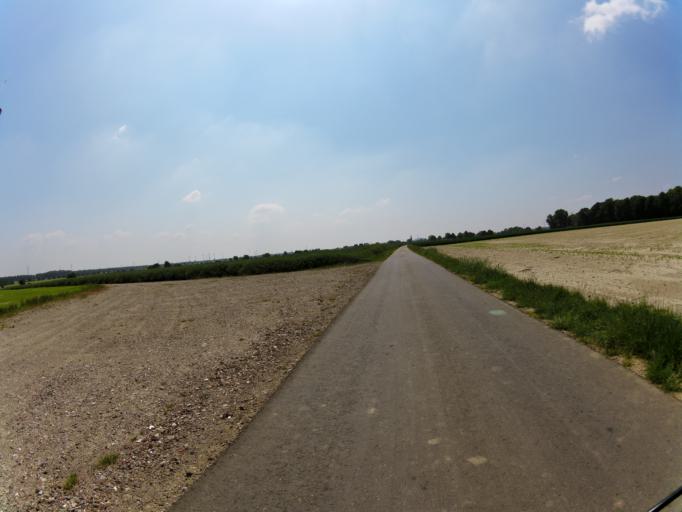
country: DE
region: North Rhine-Westphalia
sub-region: Regierungsbezirk Koln
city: Aldenhoven
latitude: 50.9130
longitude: 6.2697
